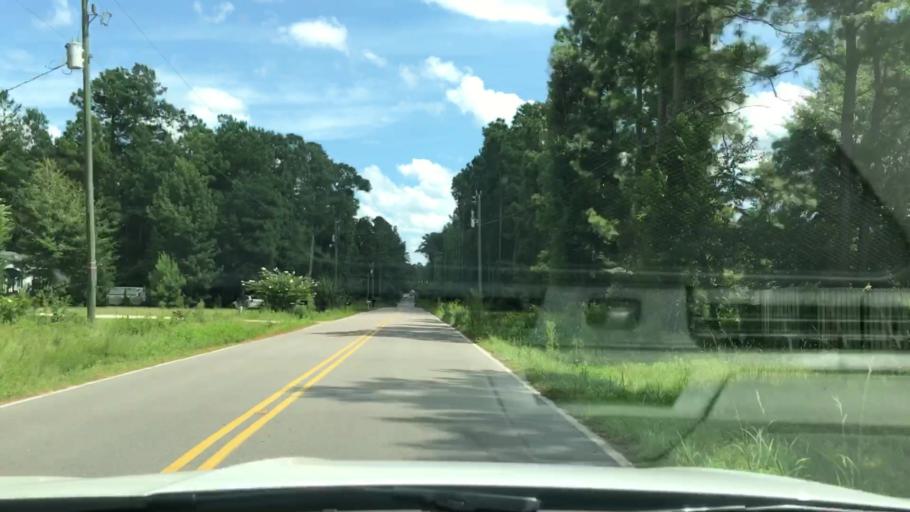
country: US
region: South Carolina
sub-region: Dorchester County
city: Summerville
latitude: 33.0362
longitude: -80.2156
